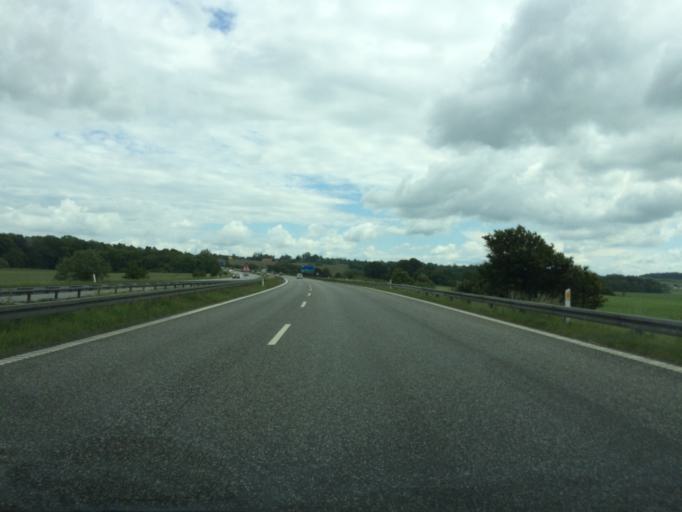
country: DK
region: Zealand
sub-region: Holbaek Kommune
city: Tollose
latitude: 55.6489
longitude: 11.7816
